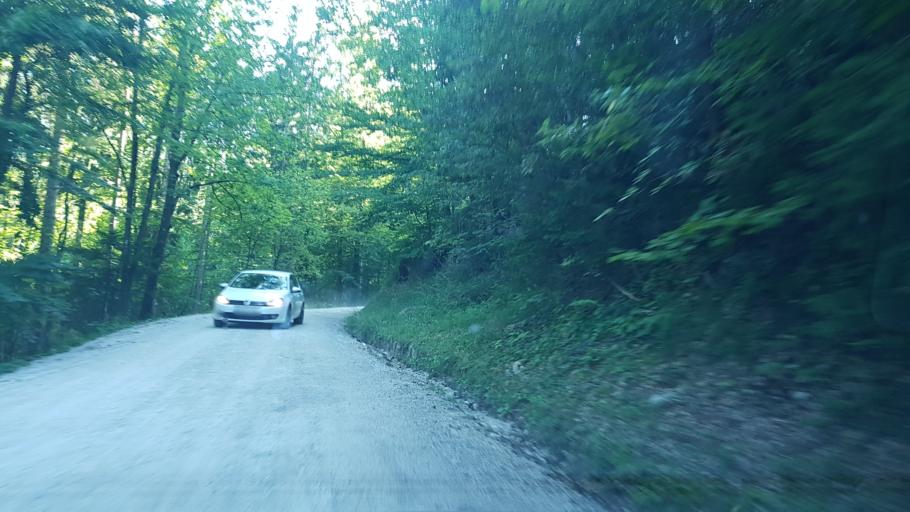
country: SI
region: Ravne na Koroskem
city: Kotlje
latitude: 46.5060
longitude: 14.9542
